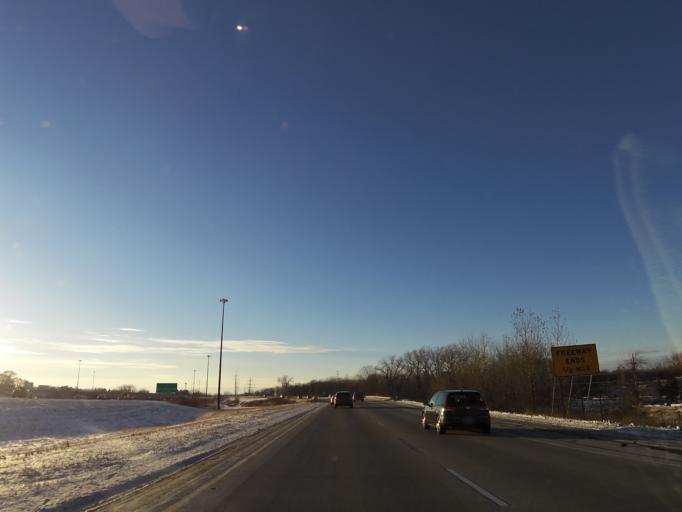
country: US
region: Minnesota
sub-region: Hennepin County
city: Eden Prairie
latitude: 44.8619
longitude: -93.4676
